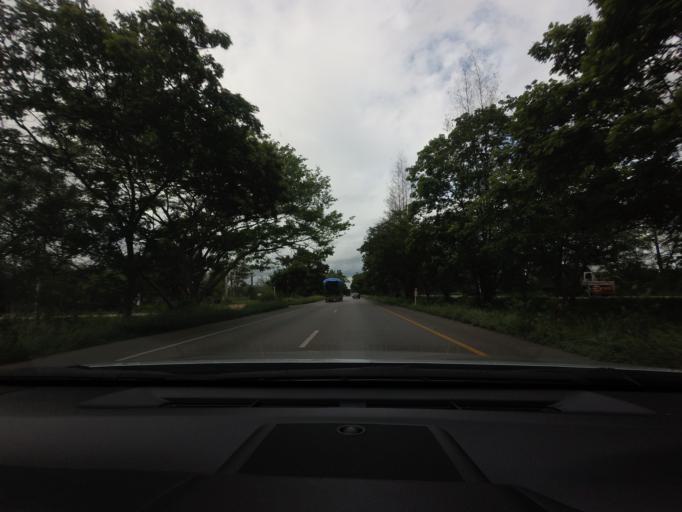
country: TH
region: Phetchaburi
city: Cha-am
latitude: 12.7070
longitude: 99.9120
